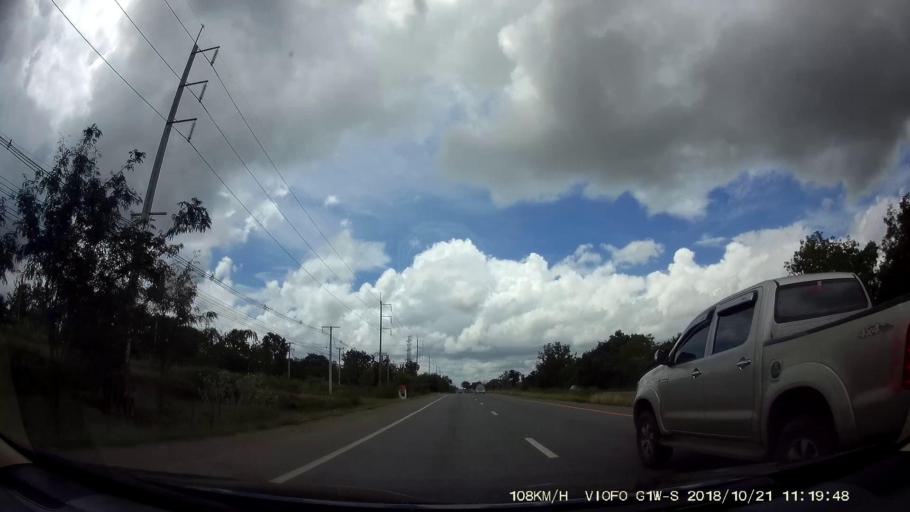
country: TH
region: Chaiyaphum
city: Chaiyaphum
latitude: 15.8639
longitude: 102.0821
